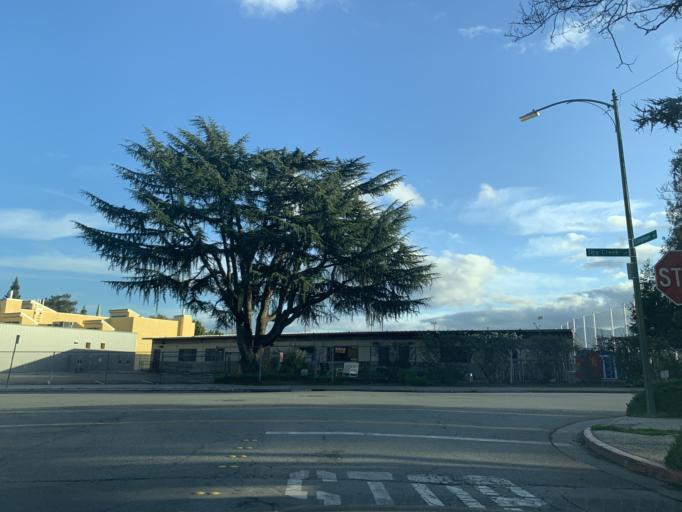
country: US
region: California
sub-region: Santa Clara County
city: Buena Vista
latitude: 37.2924
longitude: -121.8991
